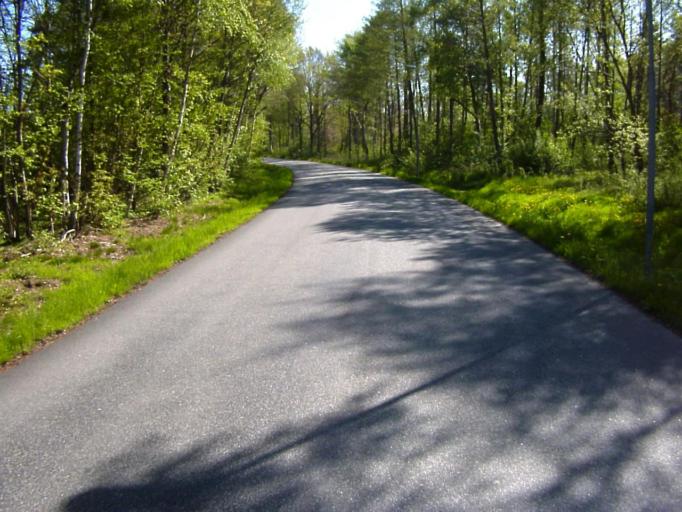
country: SE
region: Skane
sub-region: Kristianstads Kommun
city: Onnestad
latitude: 55.9388
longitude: 13.9829
